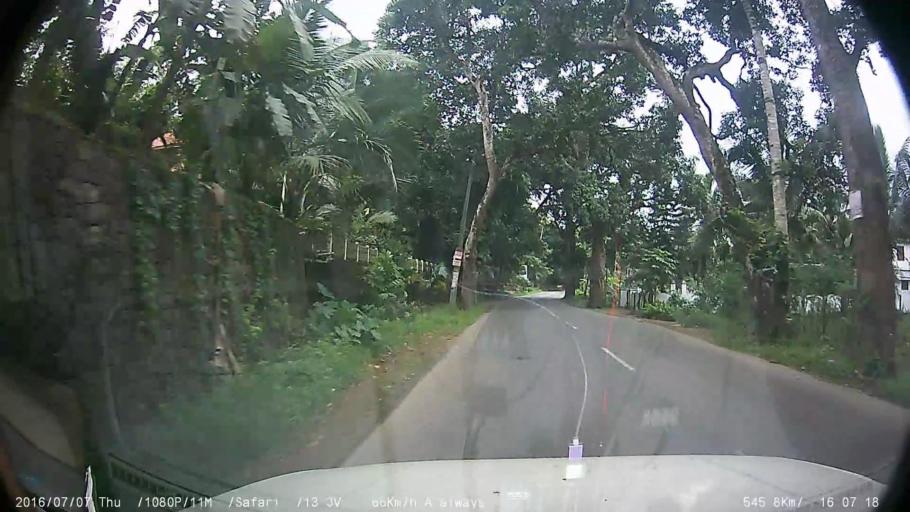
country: IN
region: Kerala
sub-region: Kottayam
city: Palackattumala
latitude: 9.8089
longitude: 76.6130
